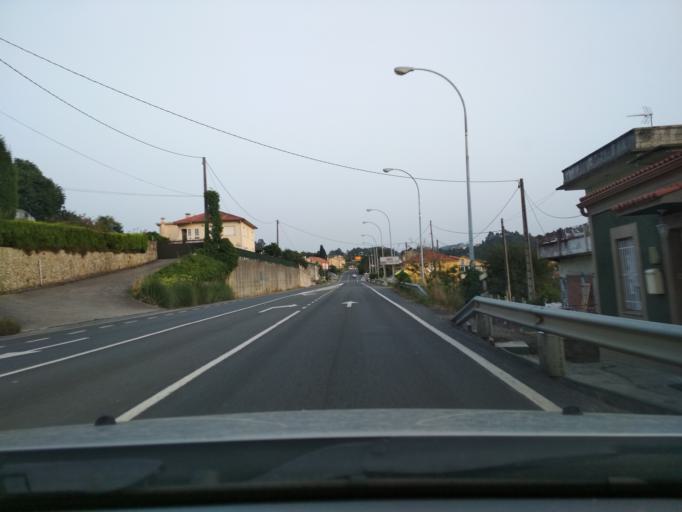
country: ES
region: Galicia
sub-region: Provincia da Coruna
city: Culleredo
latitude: 43.2822
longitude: -8.3669
